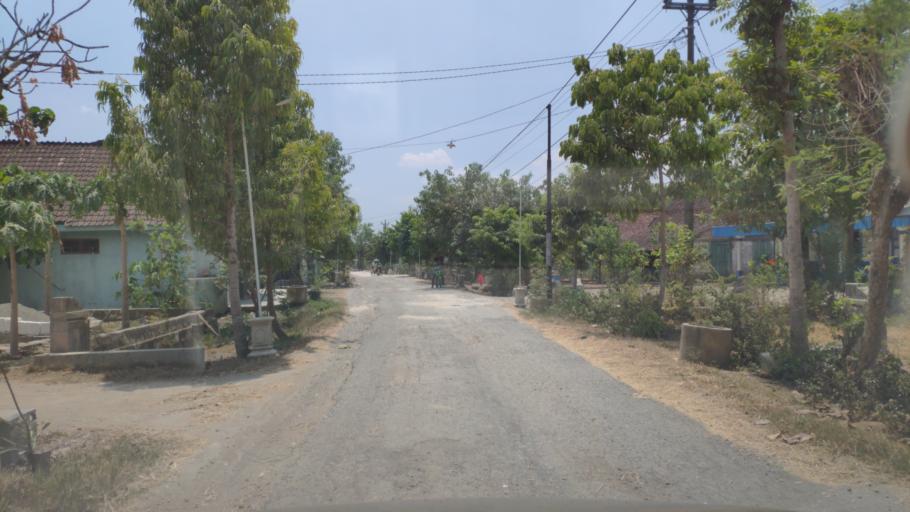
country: ID
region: Central Java
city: Klagen
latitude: -7.2109
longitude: 111.5244
